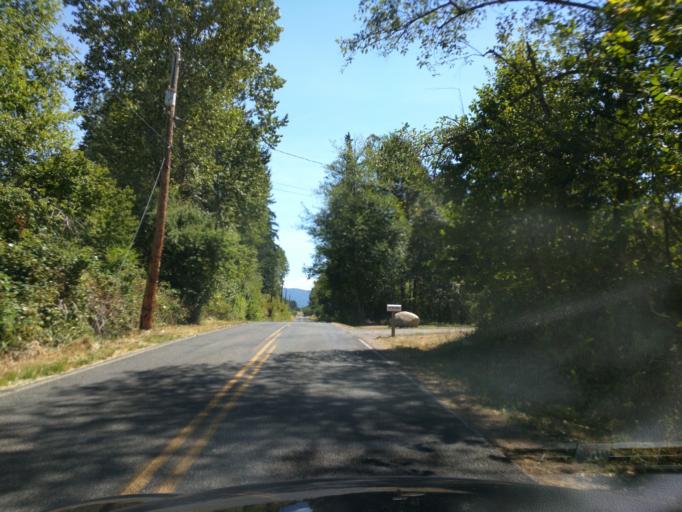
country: US
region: Washington
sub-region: Whatcom County
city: Everson
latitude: 48.8696
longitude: -122.4093
